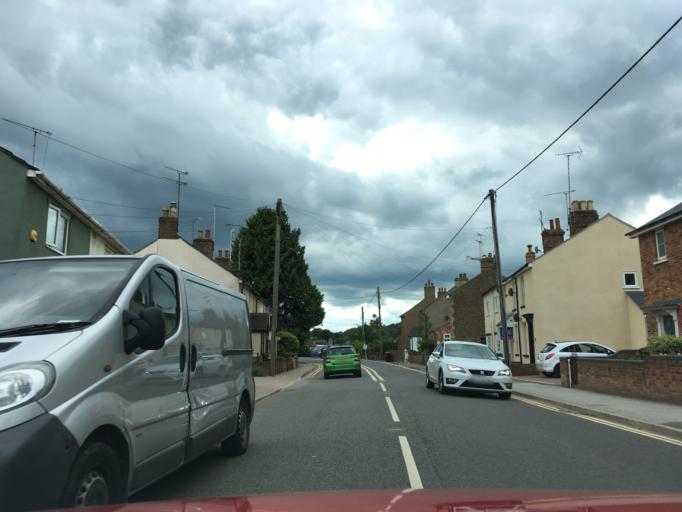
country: GB
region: England
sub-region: Central Bedfordshire
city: Leighton Buzzard
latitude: 51.9468
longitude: -0.6575
